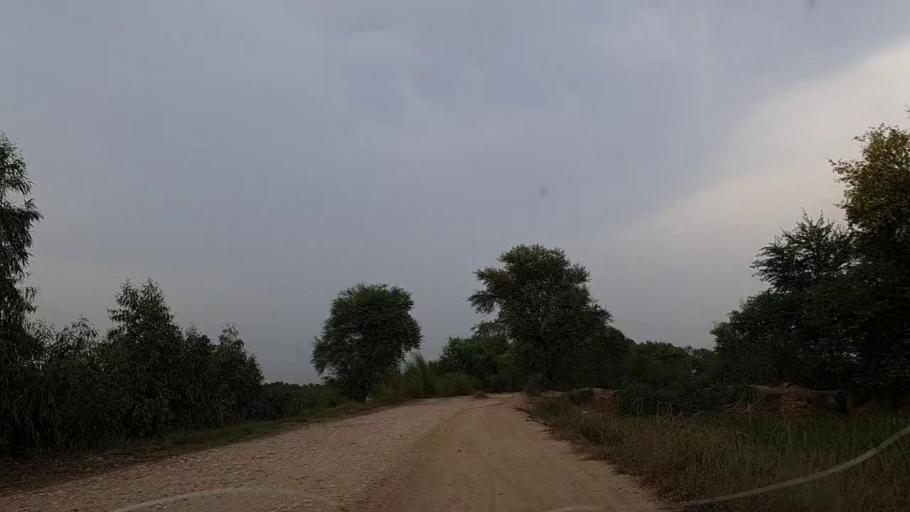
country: PK
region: Sindh
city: Mirpur Mathelo
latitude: 27.8396
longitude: 69.6187
